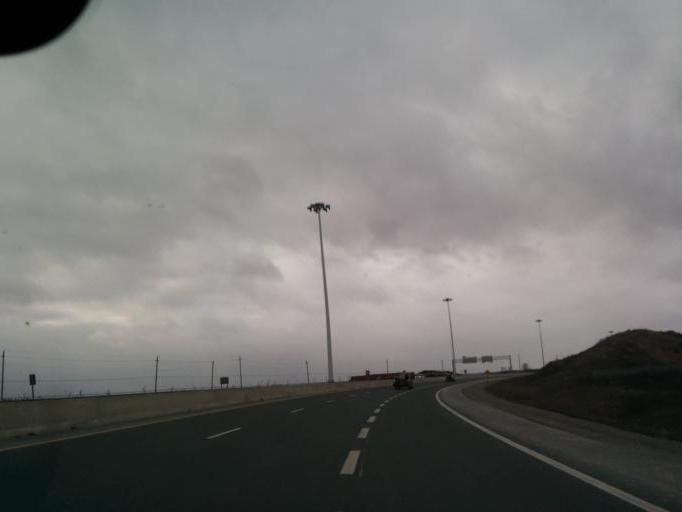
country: CA
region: Ontario
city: Brampton
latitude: 43.7414
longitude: -79.8333
